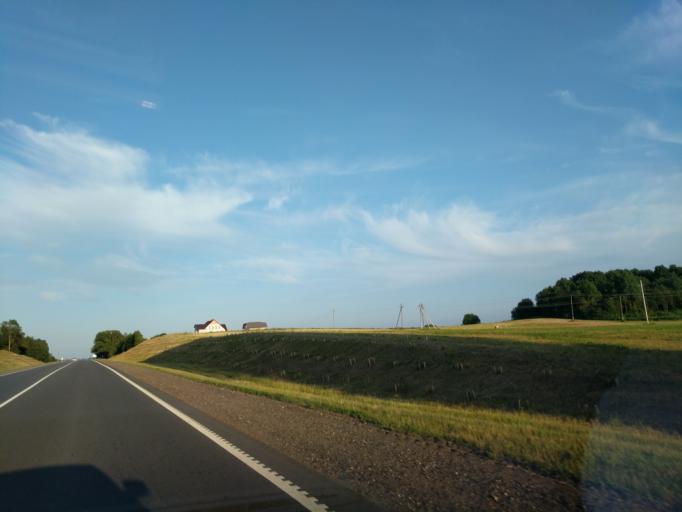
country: BY
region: Minsk
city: Syomkava
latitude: 54.1043
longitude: 27.4722
